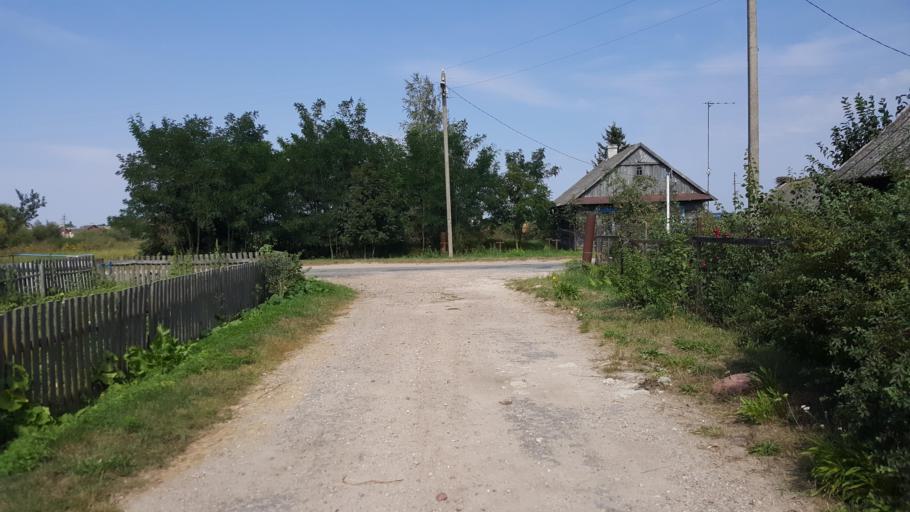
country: PL
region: Podlasie
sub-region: Powiat hajnowski
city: Czeremcha
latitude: 52.4934
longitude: 23.5735
